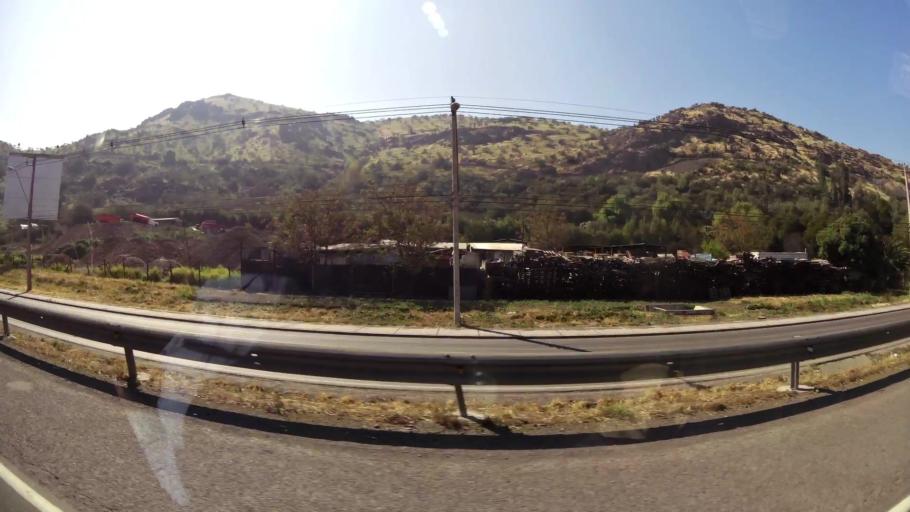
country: CL
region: Santiago Metropolitan
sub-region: Provincia de Chacabuco
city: Chicureo Abajo
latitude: -33.3459
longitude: -70.6940
